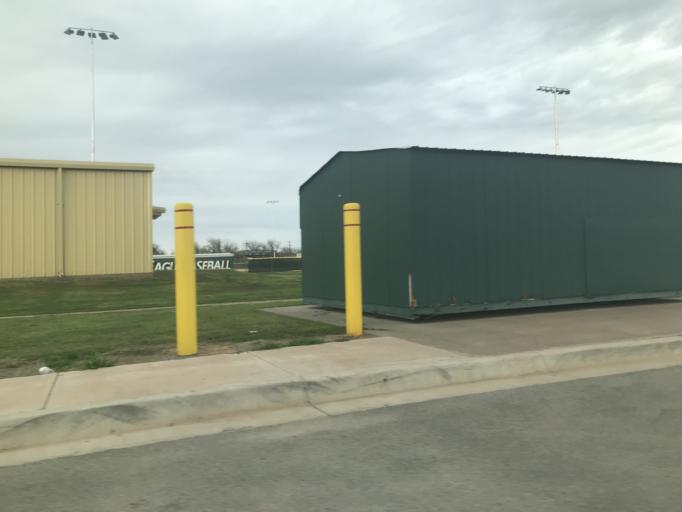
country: US
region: Texas
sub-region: Taylor County
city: Abilene
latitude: 32.4570
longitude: -99.7550
